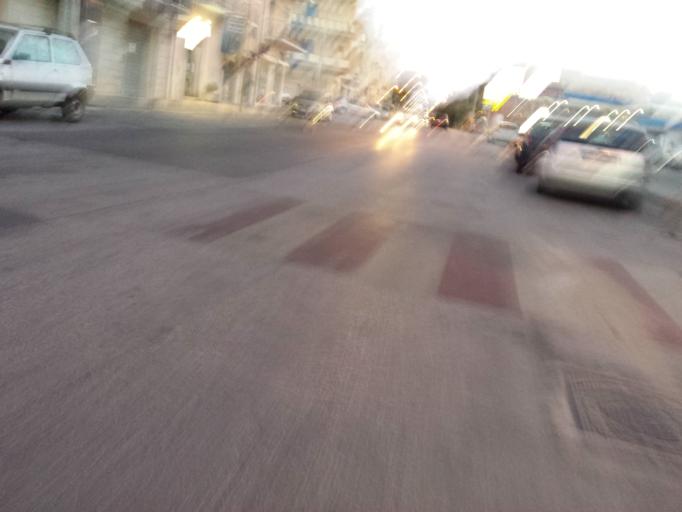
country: IT
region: Molise
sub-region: Provincia di Campobasso
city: Campobasso
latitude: 41.5692
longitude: 14.6739
